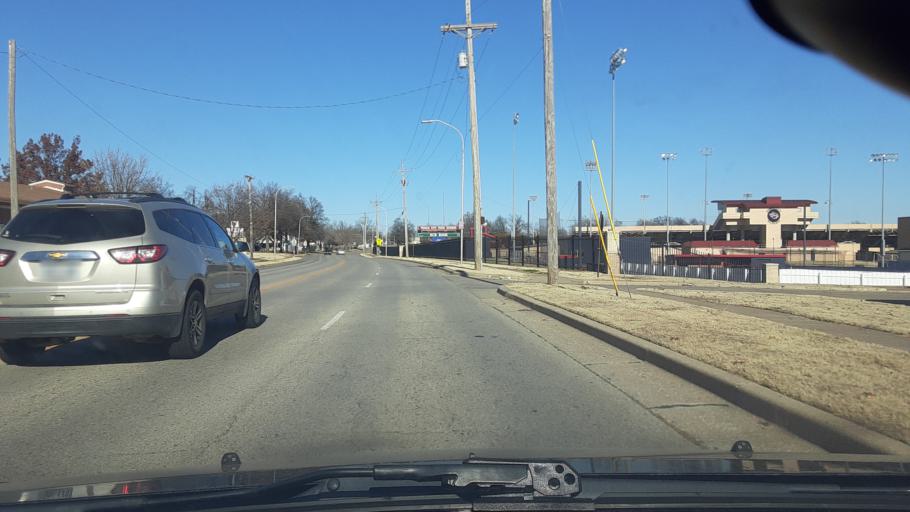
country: US
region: Oklahoma
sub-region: Kay County
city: Ponca City
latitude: 36.7157
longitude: -97.0783
